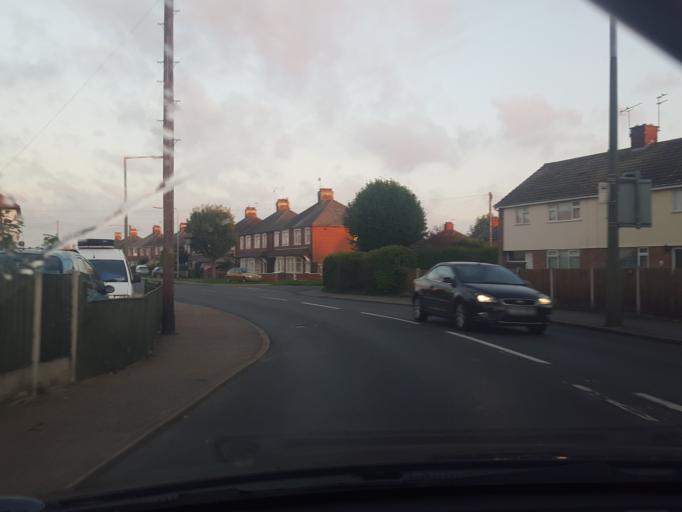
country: GB
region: England
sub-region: Essex
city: Clacton-on-Sea
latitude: 51.7967
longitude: 1.1328
